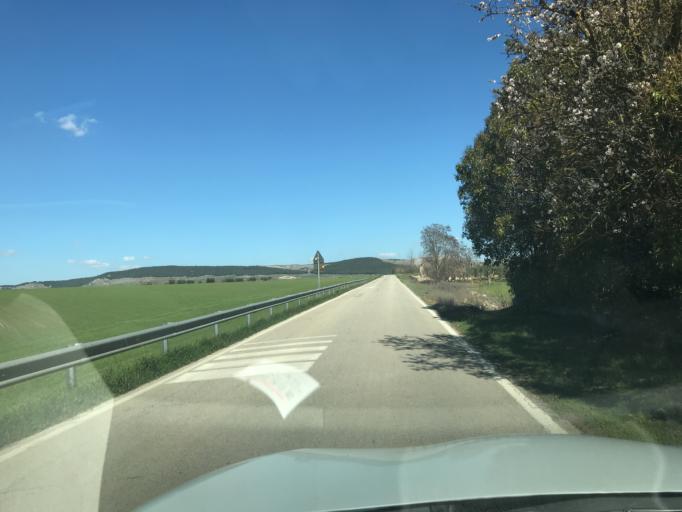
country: IT
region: Apulia
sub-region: Provincia di Bari
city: Gravina in Puglia
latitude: 40.8496
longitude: 16.4283
